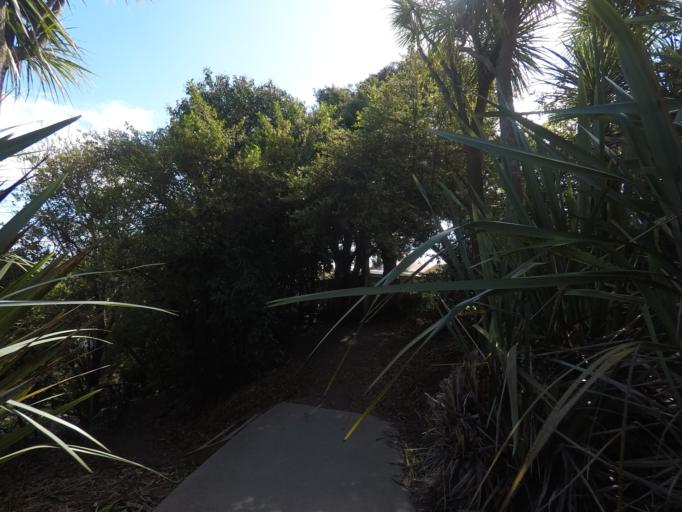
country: NZ
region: Auckland
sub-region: Auckland
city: Rosebank
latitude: -36.8555
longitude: 174.7126
